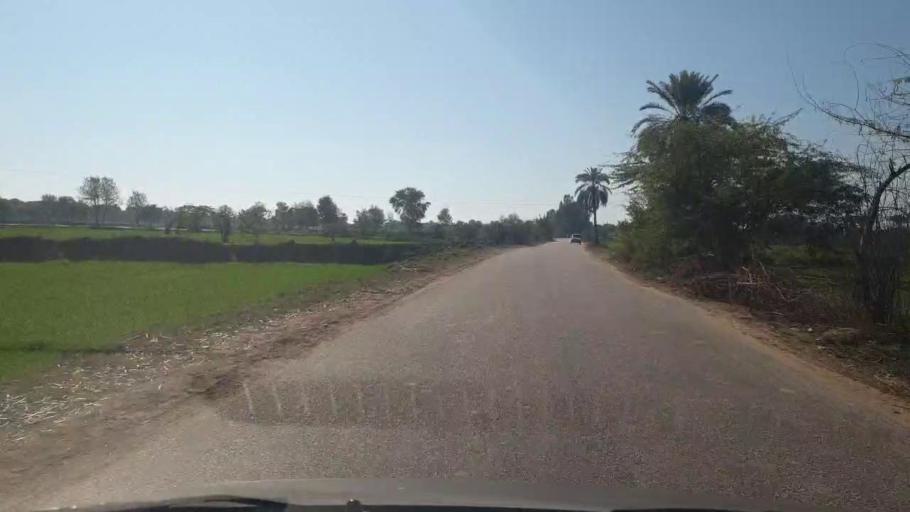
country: PK
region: Sindh
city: Bozdar
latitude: 27.1007
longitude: 68.6302
